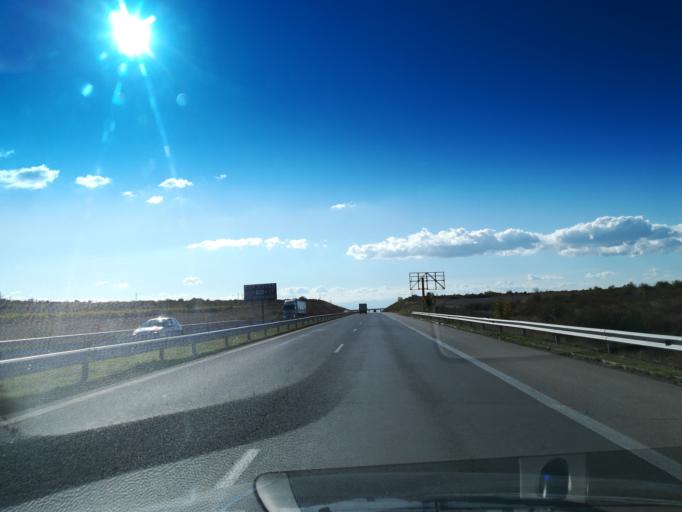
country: BG
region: Stara Zagora
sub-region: Obshtina Chirpan
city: Chirpan
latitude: 42.2319
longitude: 25.3578
